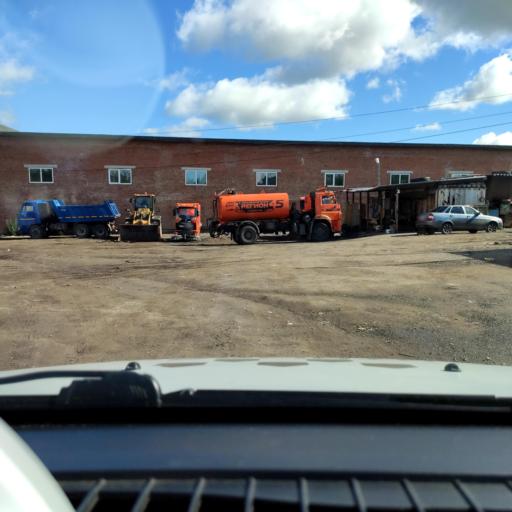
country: RU
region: Perm
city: Perm
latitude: 57.9733
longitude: 56.2897
